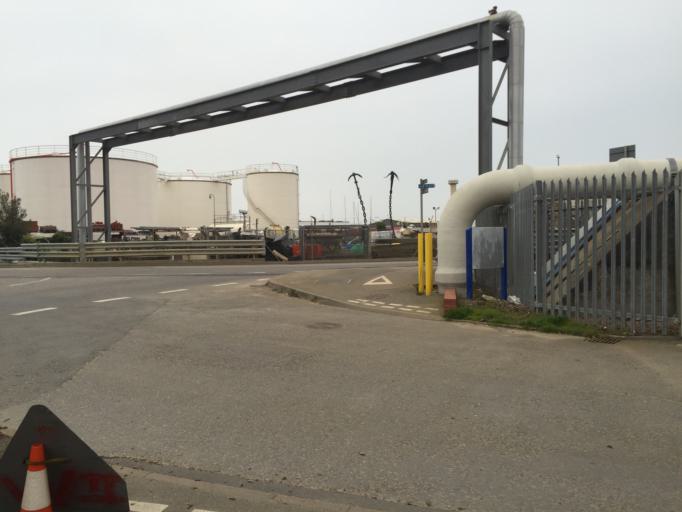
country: JE
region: St Helier
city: Saint Helier
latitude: 49.1740
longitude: -2.1089
